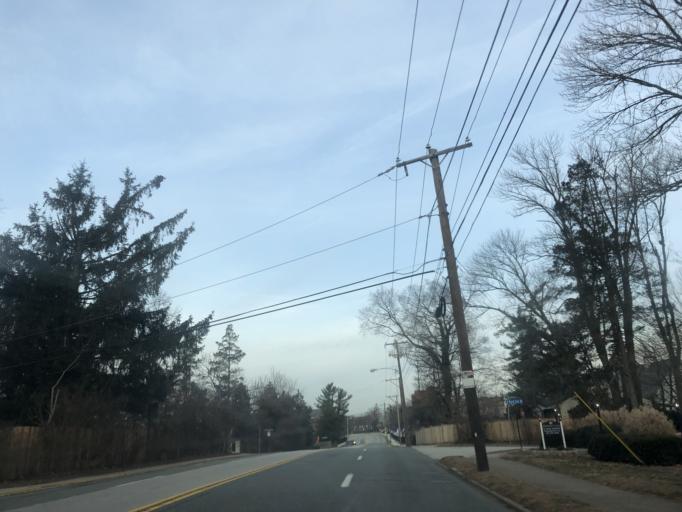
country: US
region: Pennsylvania
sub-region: Delaware County
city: Radnor
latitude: 40.0310
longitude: -75.3353
